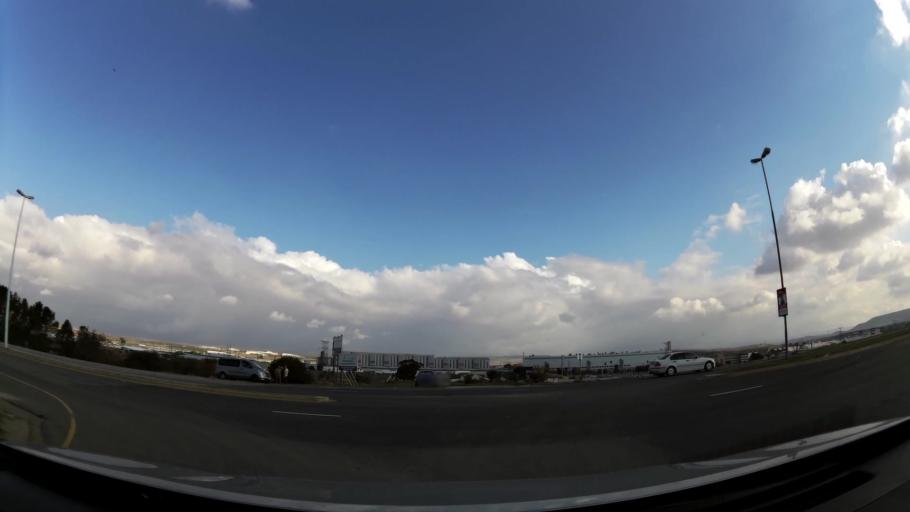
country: ZA
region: Eastern Cape
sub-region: Nelson Mandela Bay Metropolitan Municipality
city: Uitenhage
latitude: -33.7802
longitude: 25.4241
